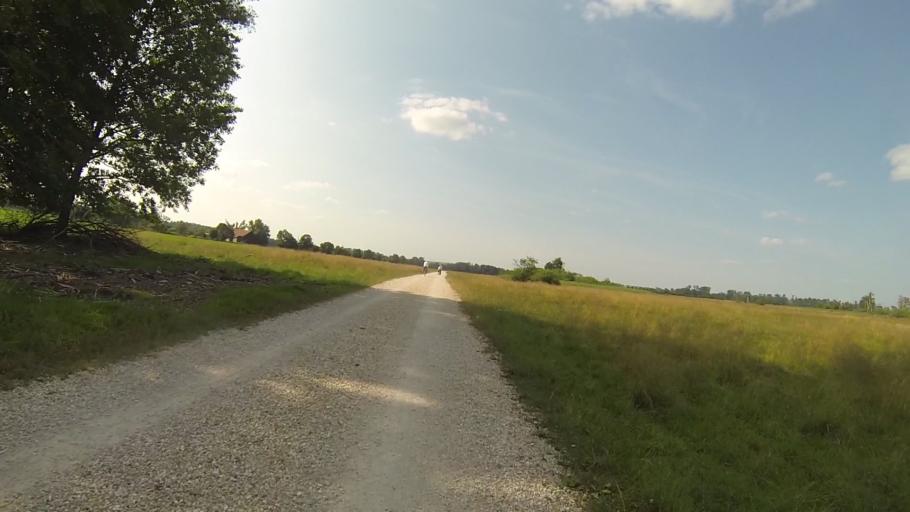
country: DE
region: Baden-Wuerttemberg
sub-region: Tuebingen Region
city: Rammingen
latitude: 48.4805
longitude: 10.1901
